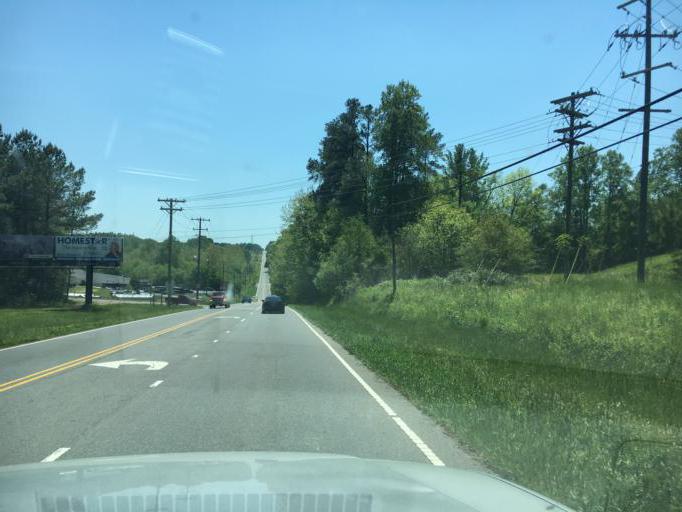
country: US
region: North Carolina
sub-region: Cleveland County
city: Shelby
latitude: 35.2452
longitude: -81.5668
